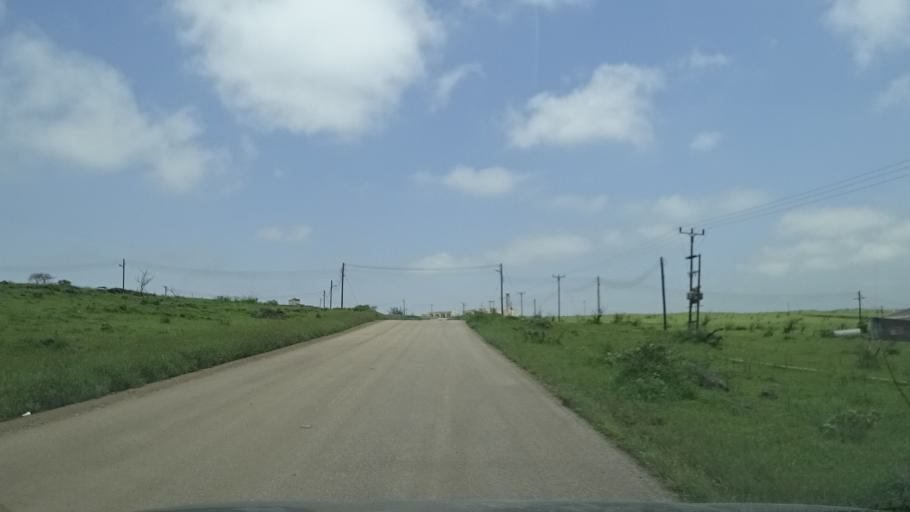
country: OM
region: Zufar
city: Salalah
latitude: 17.2291
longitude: 54.2102
